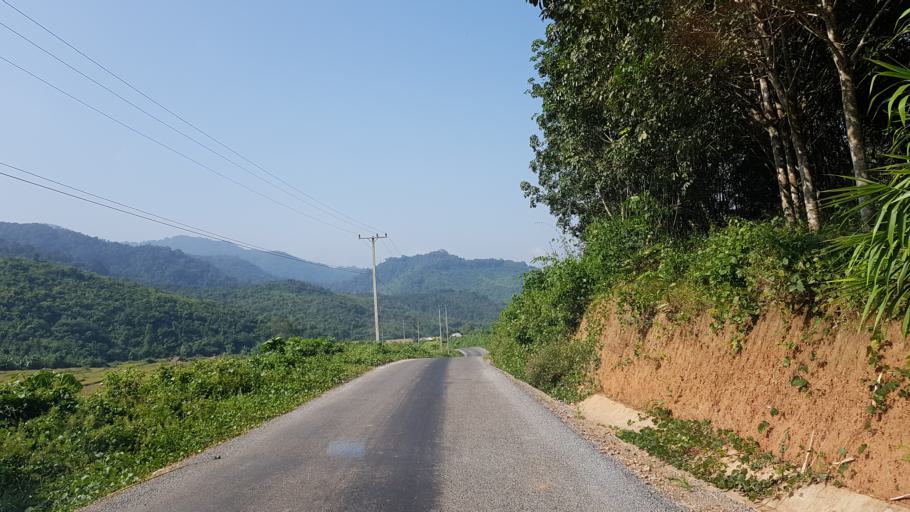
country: LA
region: Oudomxai
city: Muang Xay
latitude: 20.7136
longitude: 102.0655
